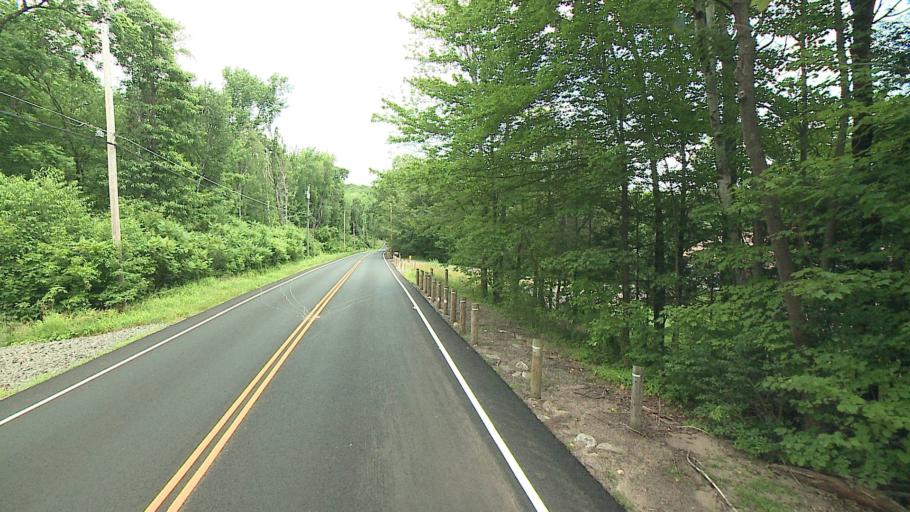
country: US
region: Massachusetts
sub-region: Hampden County
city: Granville
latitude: 42.0312
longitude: -72.8853
